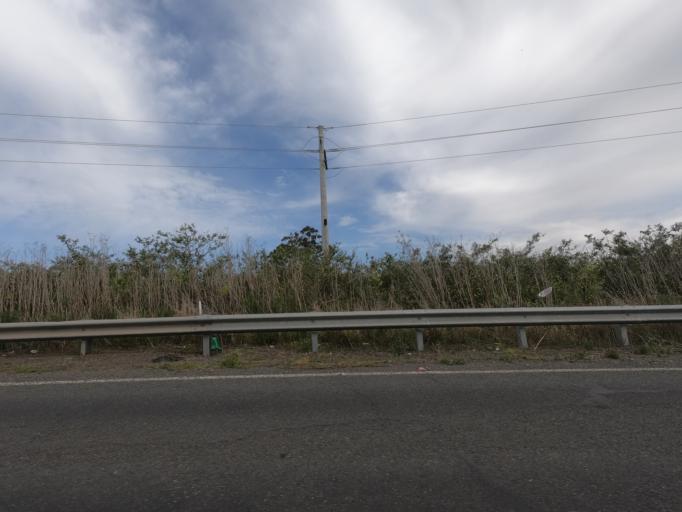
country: AU
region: New South Wales
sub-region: Wollongong
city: Dapto
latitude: -34.4802
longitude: 150.7794
